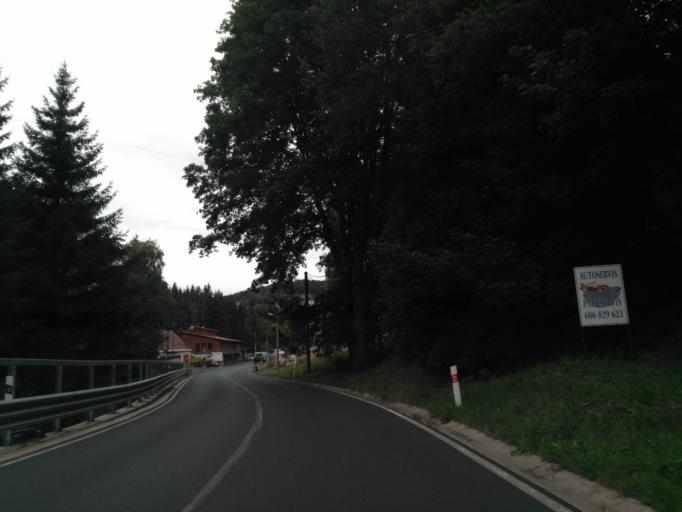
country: DE
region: Saxony
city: Johanngeorgenstadt
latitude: 50.4179
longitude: 12.7337
